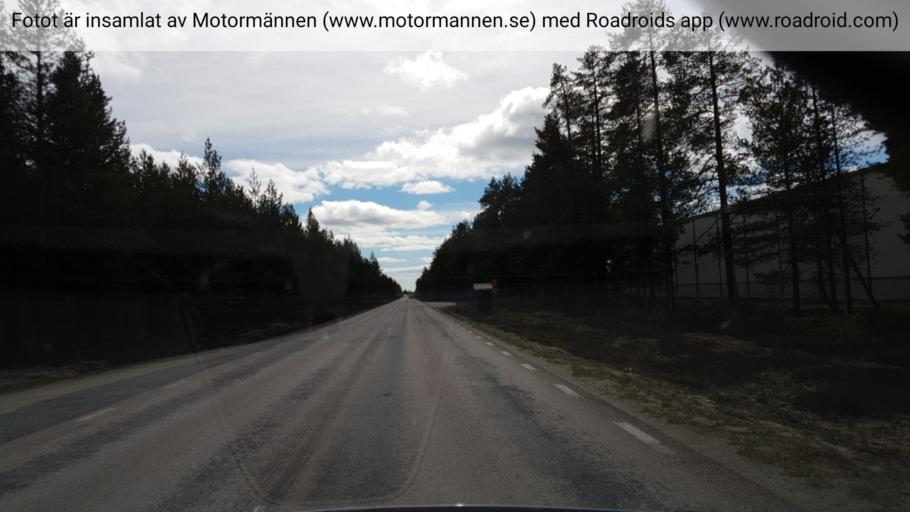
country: SE
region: Vaesternorrland
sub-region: OErnskoeldsviks Kommun
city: Husum
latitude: 63.4586
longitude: 18.9568
